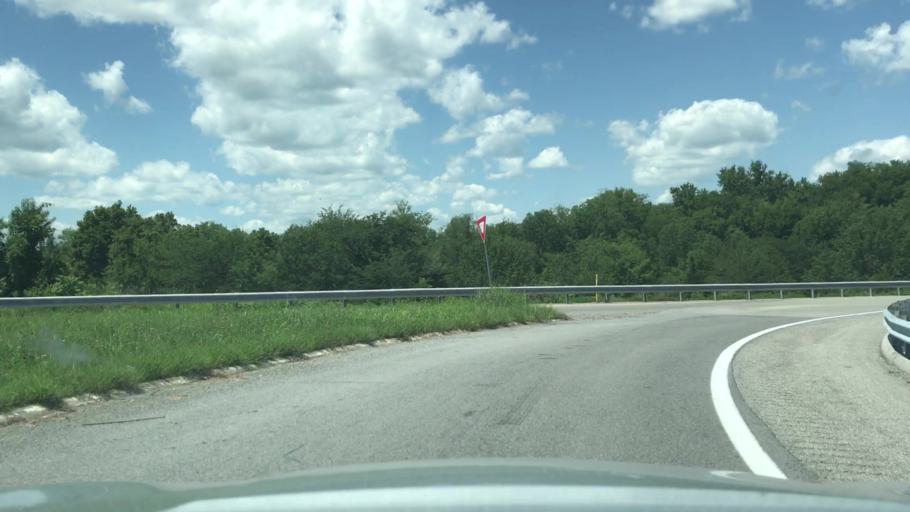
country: US
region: Kentucky
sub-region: Christian County
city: Hopkinsville
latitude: 36.8955
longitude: -87.4708
